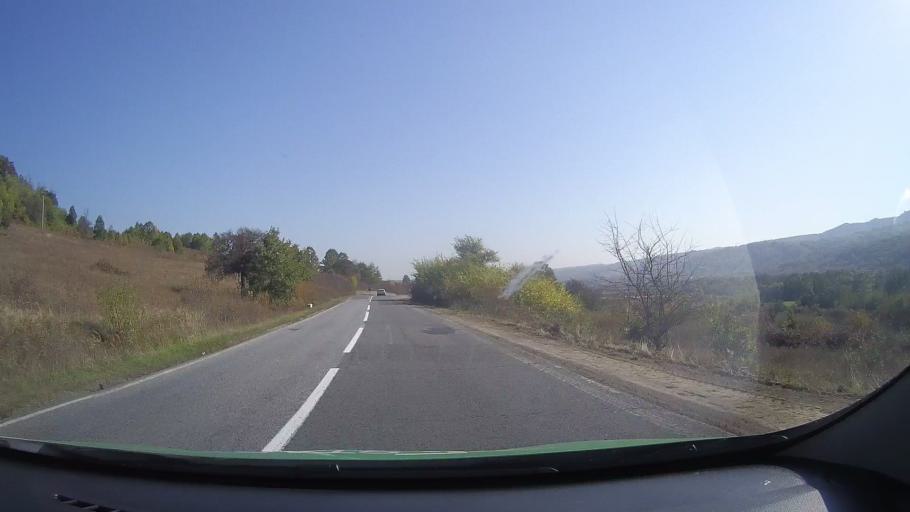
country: RO
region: Hunedoara
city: Lapugiu de Jos
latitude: 45.8879
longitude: 22.4619
